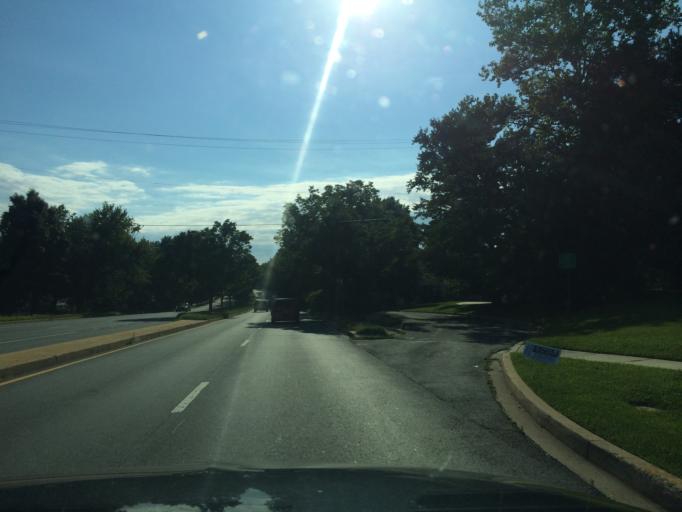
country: US
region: Maryland
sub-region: Montgomery County
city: Rossmoor
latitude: 39.0995
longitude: -77.0998
